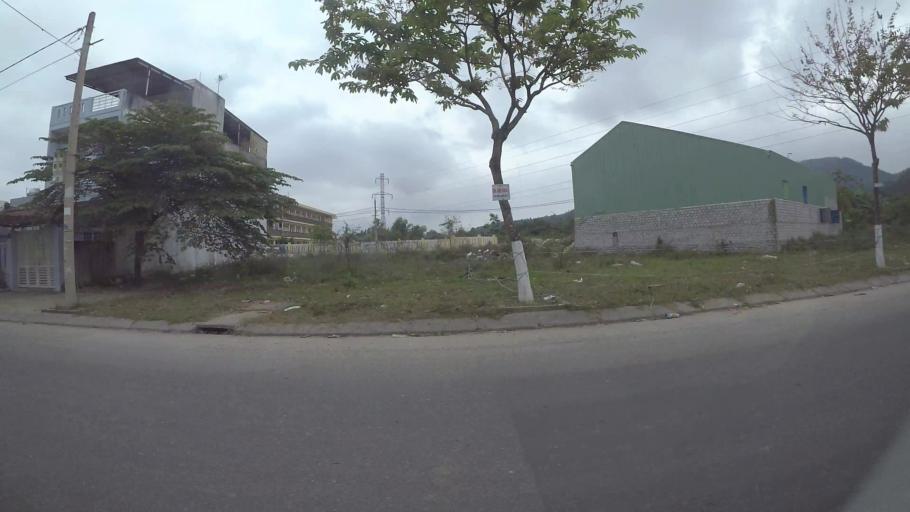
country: VN
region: Da Nang
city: Thanh Khe
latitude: 16.0433
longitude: 108.1751
